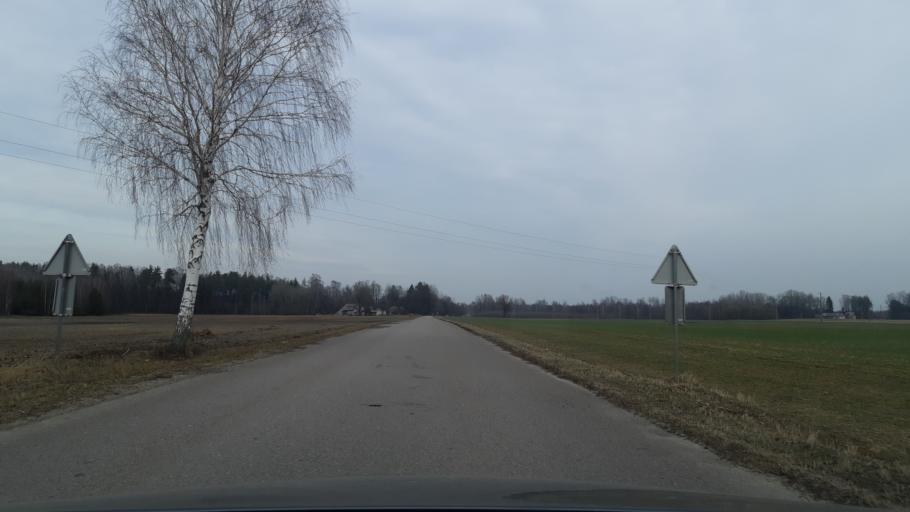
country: LT
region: Marijampoles apskritis
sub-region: Marijampole Municipality
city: Marijampole
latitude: 54.7284
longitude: 23.3370
